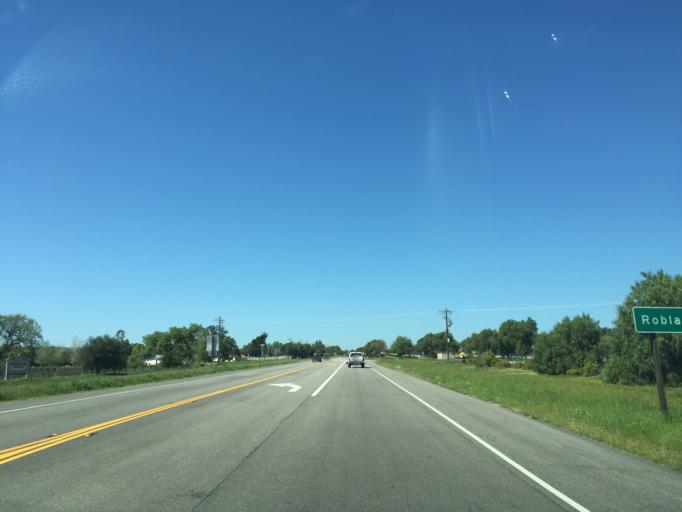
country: US
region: California
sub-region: Santa Barbara County
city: Los Olivos
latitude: 34.6493
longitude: -120.0942
